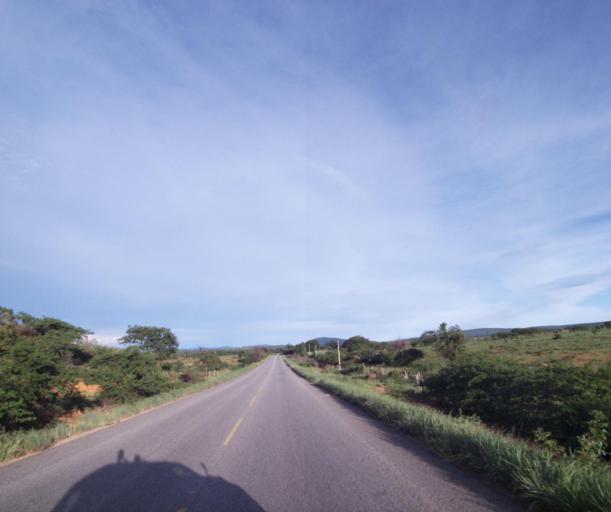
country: BR
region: Bahia
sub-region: Caetite
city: Caetite
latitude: -14.1723
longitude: -42.1986
